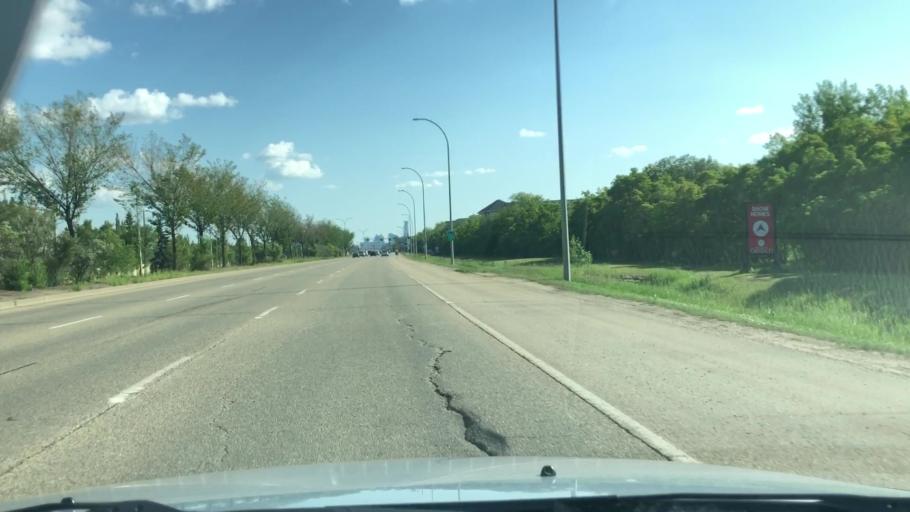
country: CA
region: Alberta
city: Edmonton
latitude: 53.6054
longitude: -113.4920
